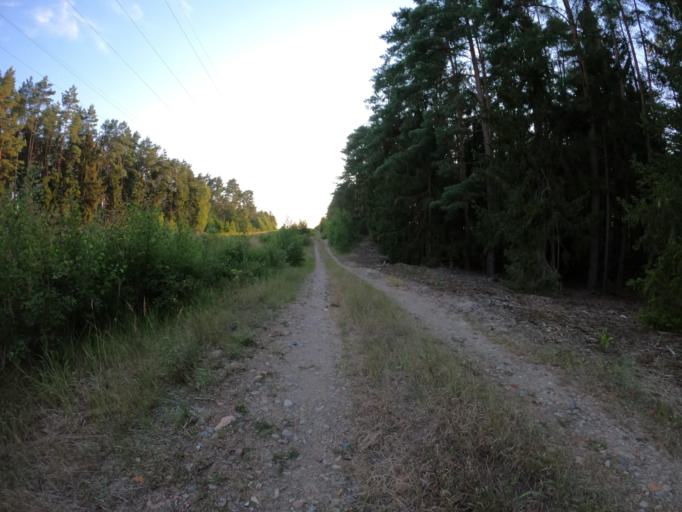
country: DE
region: Brandenburg
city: Templin
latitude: 53.1655
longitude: 13.5209
